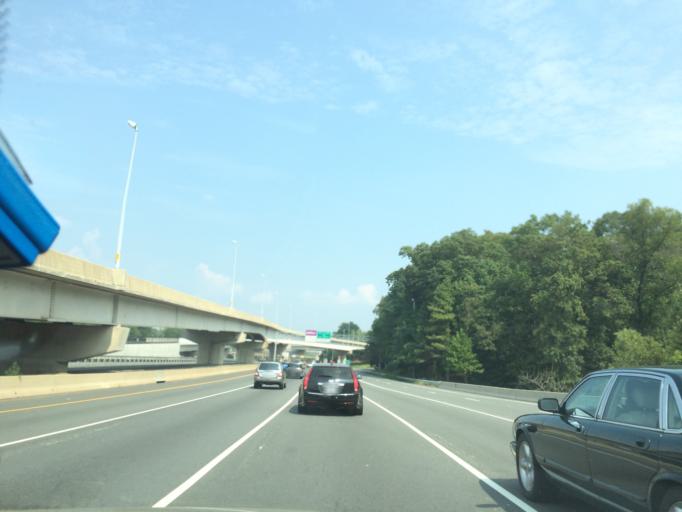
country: US
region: Virginia
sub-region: Fairfax County
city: Tysons Corner
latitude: 38.9323
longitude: -77.2527
